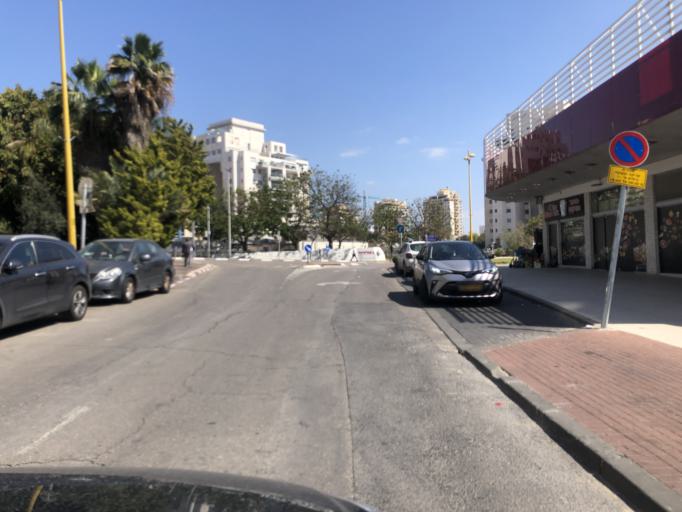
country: IL
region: Tel Aviv
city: Holon
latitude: 32.0031
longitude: 34.7672
